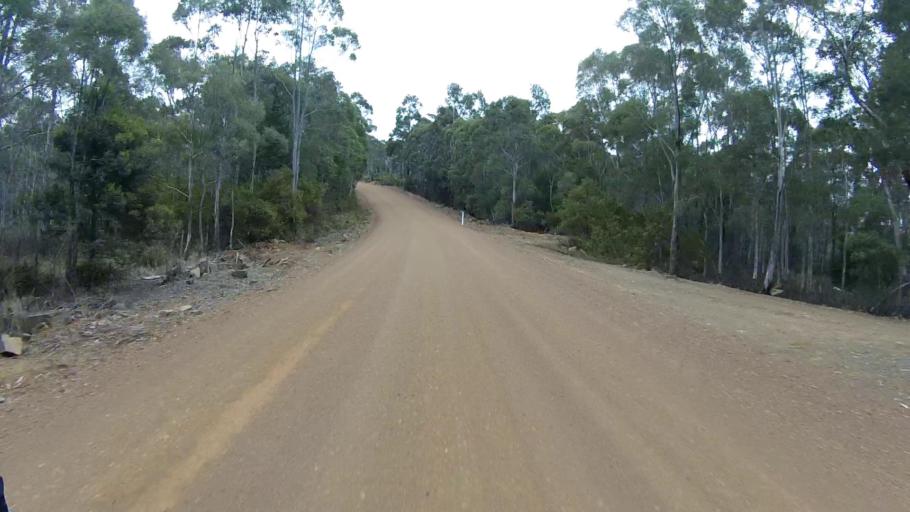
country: AU
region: Tasmania
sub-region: Sorell
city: Sorell
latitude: -42.5914
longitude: 147.8862
